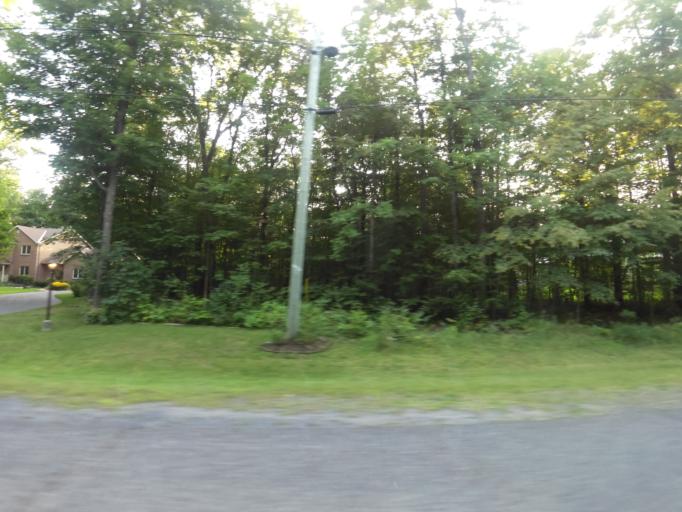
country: CA
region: Ontario
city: Clarence-Rockland
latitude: 45.5005
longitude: -75.4310
